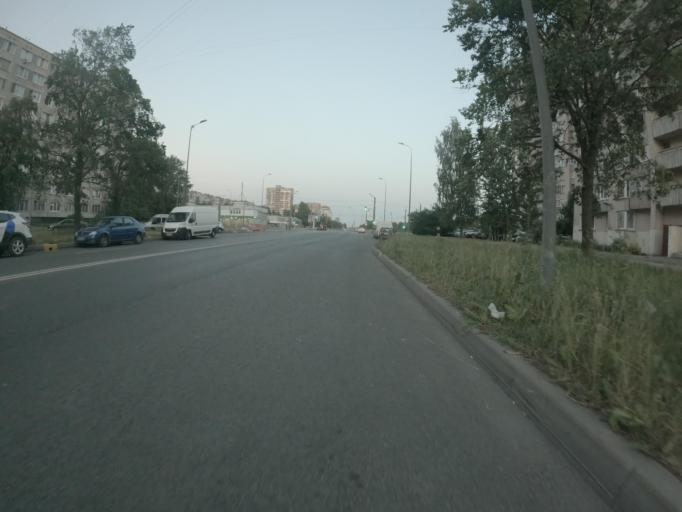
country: RU
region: St.-Petersburg
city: Krasnogvargeisky
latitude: 59.9160
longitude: 30.4842
